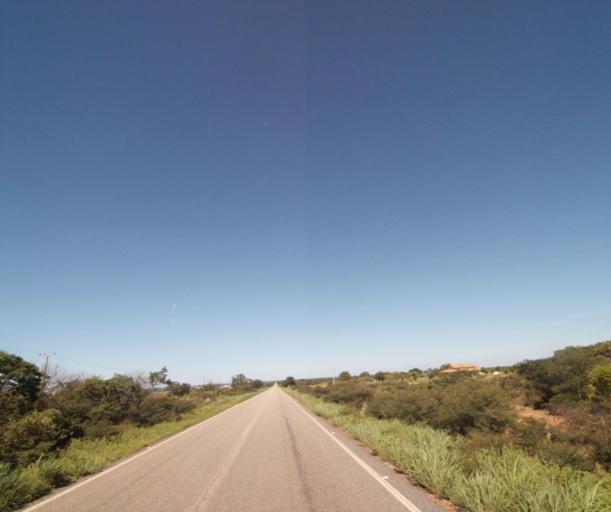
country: BR
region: Bahia
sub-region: Palmas De Monte Alto
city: Palmas de Monte Alto
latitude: -14.2560
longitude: -43.2430
